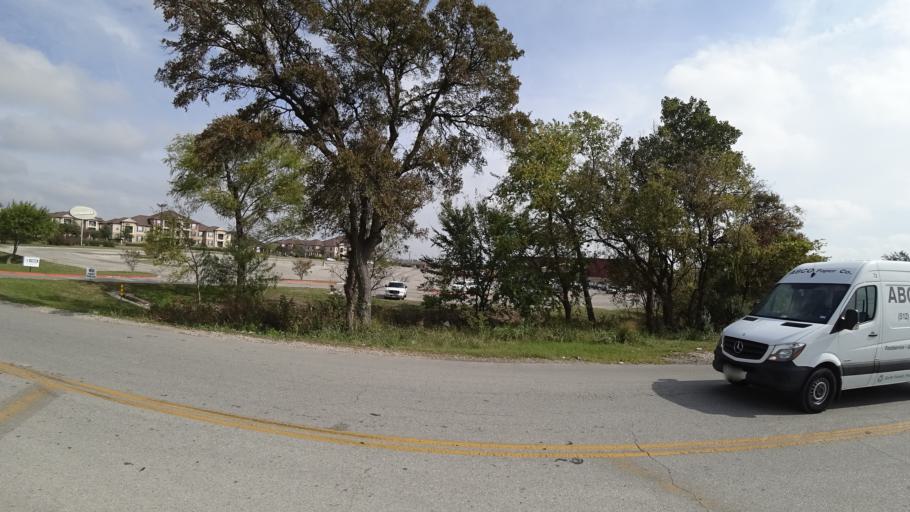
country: US
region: Texas
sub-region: Travis County
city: Windemere
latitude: 30.4554
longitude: -97.6642
